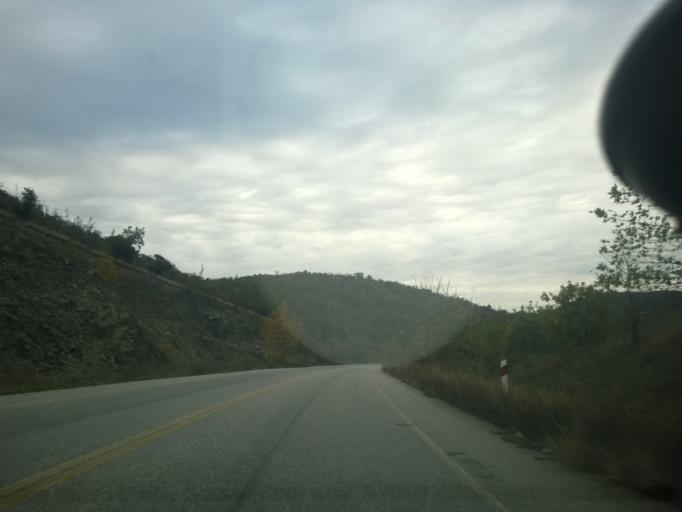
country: GR
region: Central Macedonia
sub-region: Nomos Pellis
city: Profitis Ilias
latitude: 40.8408
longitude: 22.1163
